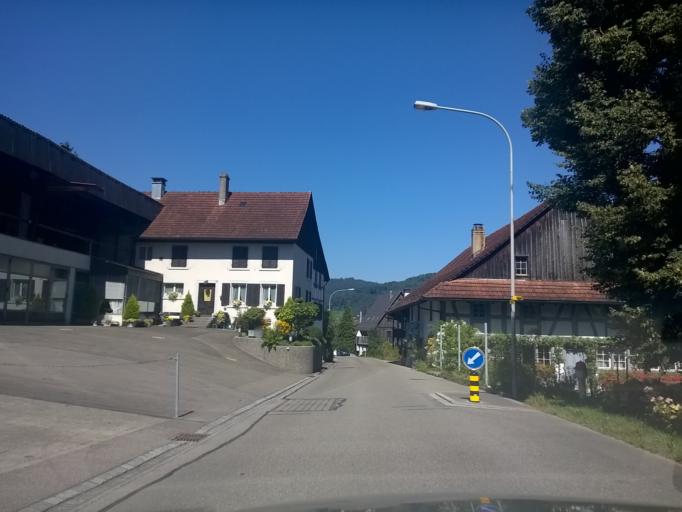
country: CH
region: Zurich
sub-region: Bezirk Winterthur
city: Pfungen
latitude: 47.5110
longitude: 8.6420
